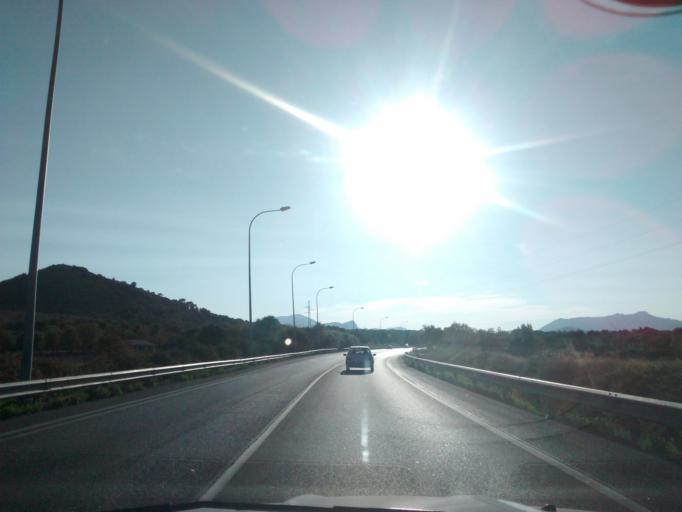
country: ES
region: Balearic Islands
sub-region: Illes Balears
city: Alcudia
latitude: 39.8418
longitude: 3.1029
